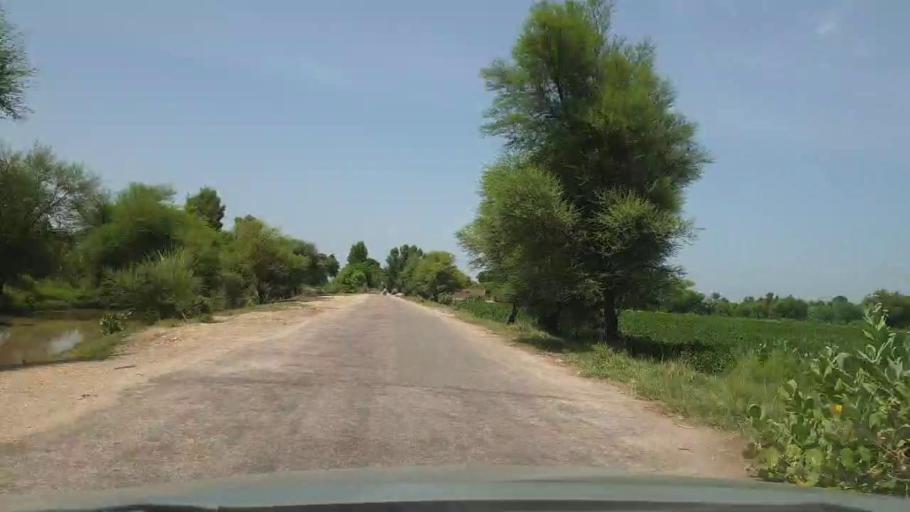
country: PK
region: Sindh
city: Pano Aqil
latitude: 27.6894
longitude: 69.1108
